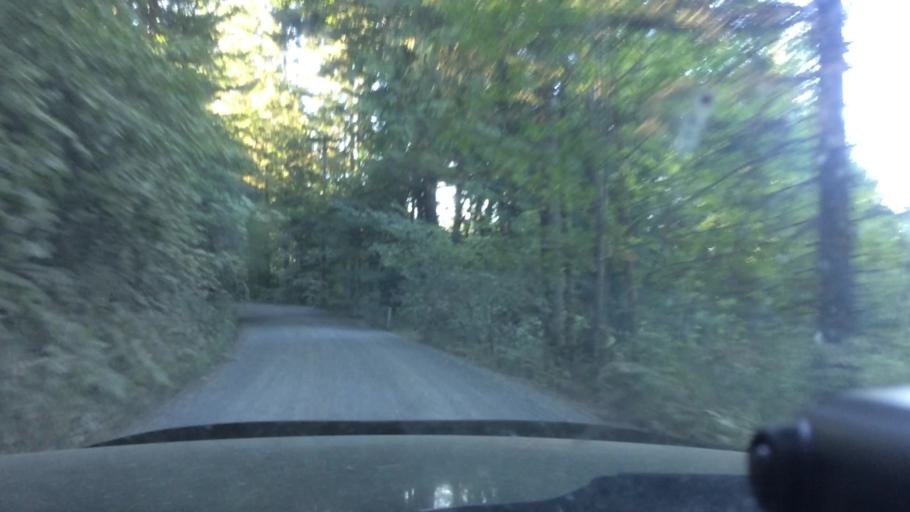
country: US
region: Oregon
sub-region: Yamhill County
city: Newberg
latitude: 45.3583
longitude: -122.9735
